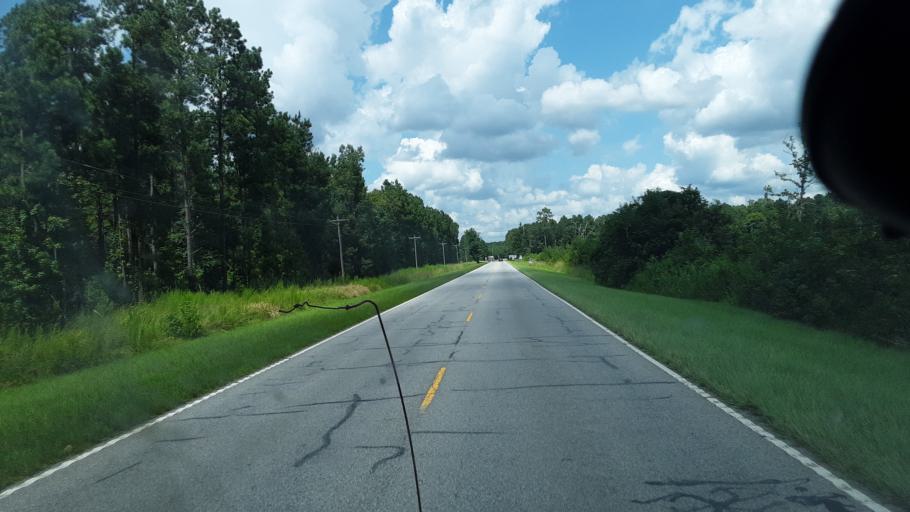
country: US
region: South Carolina
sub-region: Florence County
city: Johnsonville
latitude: 33.6239
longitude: -79.4323
